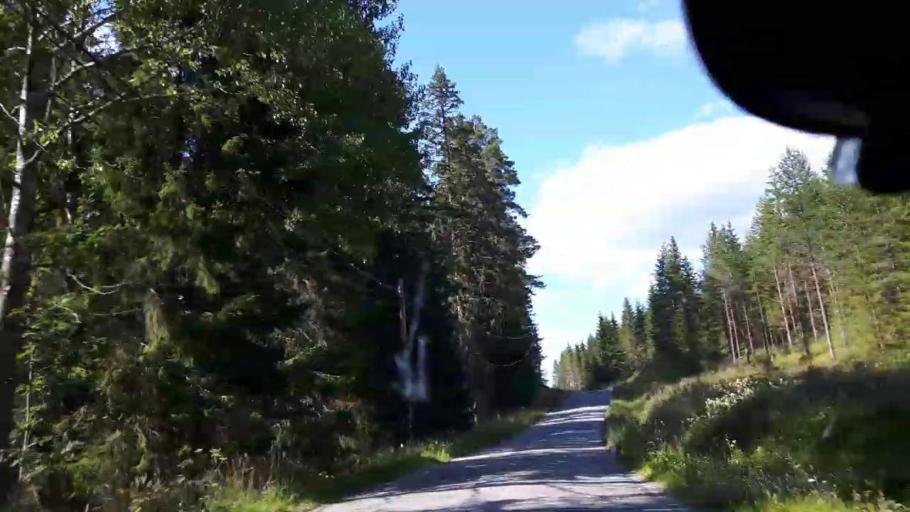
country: SE
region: Jaemtland
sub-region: Braecke Kommun
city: Braecke
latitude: 62.8641
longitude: 15.2729
